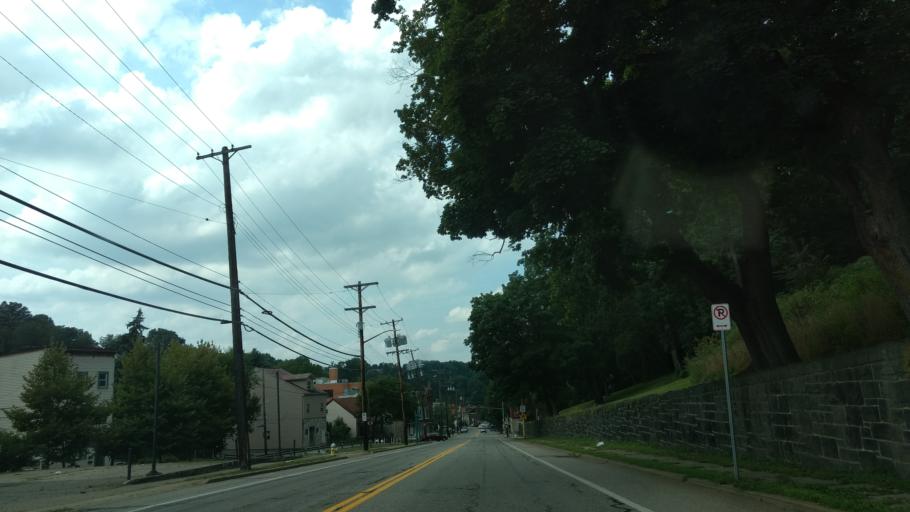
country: US
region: Pennsylvania
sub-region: Allegheny County
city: Bellevue
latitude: 40.4725
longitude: -80.0279
